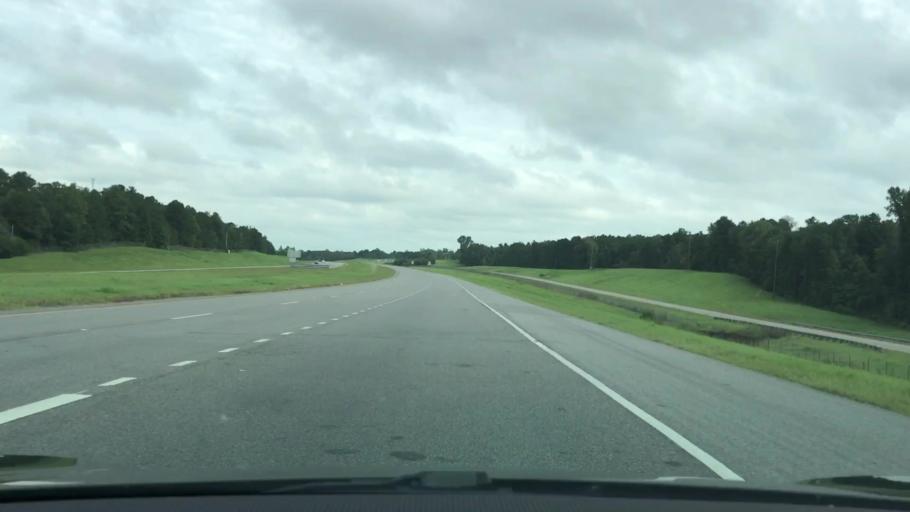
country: US
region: Alabama
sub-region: Montgomery County
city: Pike Road
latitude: 32.3414
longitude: -86.0635
